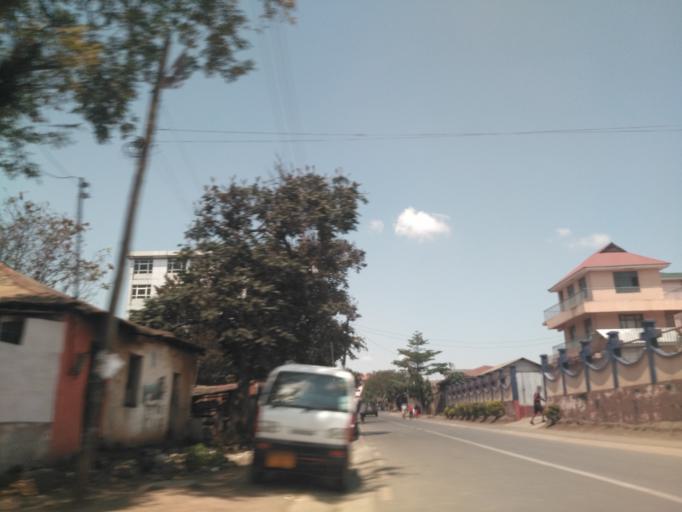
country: TZ
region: Arusha
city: Arusha
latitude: -3.3670
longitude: 36.6878
